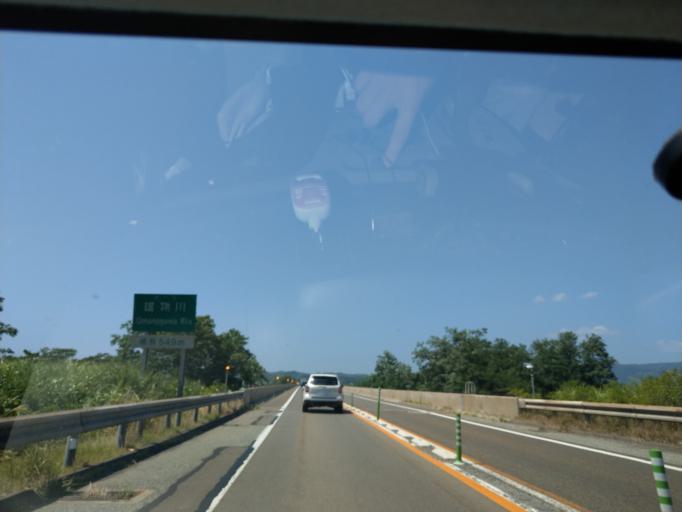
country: JP
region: Akita
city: Omagari
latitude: 39.4011
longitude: 140.4692
